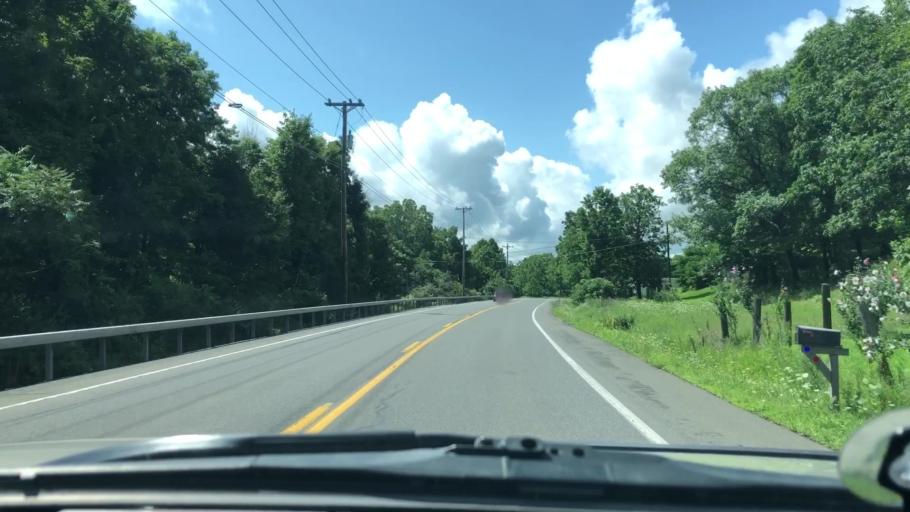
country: US
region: New York
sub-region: Greene County
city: Palenville
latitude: 42.2300
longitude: -73.9828
